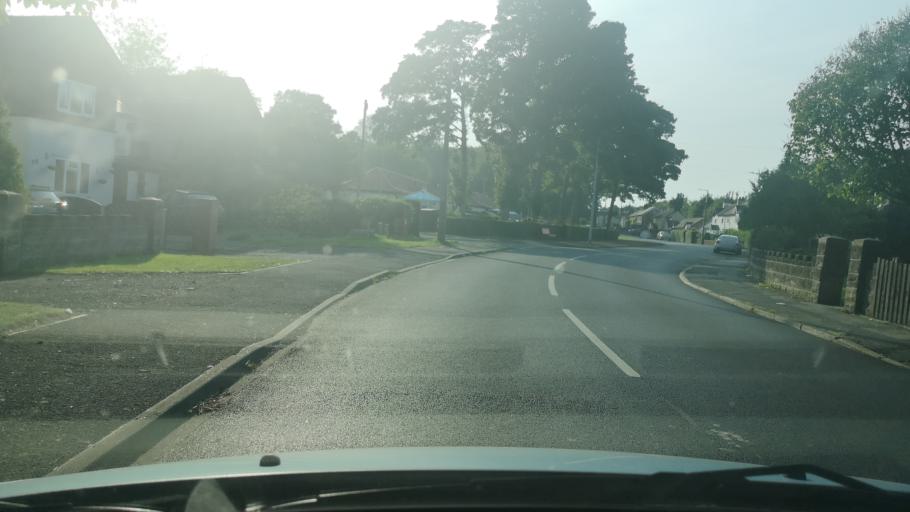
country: GB
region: England
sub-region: North Lincolnshire
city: Scunthorpe
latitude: 53.5845
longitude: -0.6573
